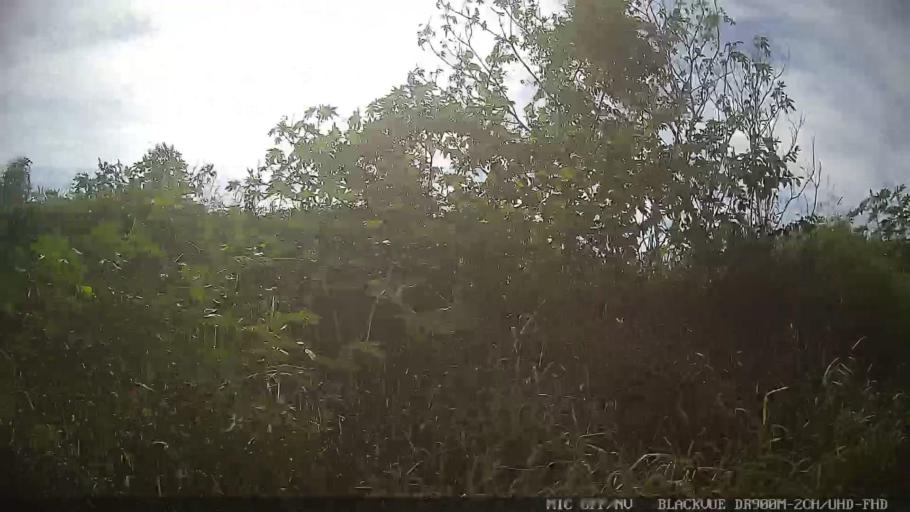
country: BR
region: Sao Paulo
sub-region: Jarinu
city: Jarinu
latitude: -23.0351
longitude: -46.6405
